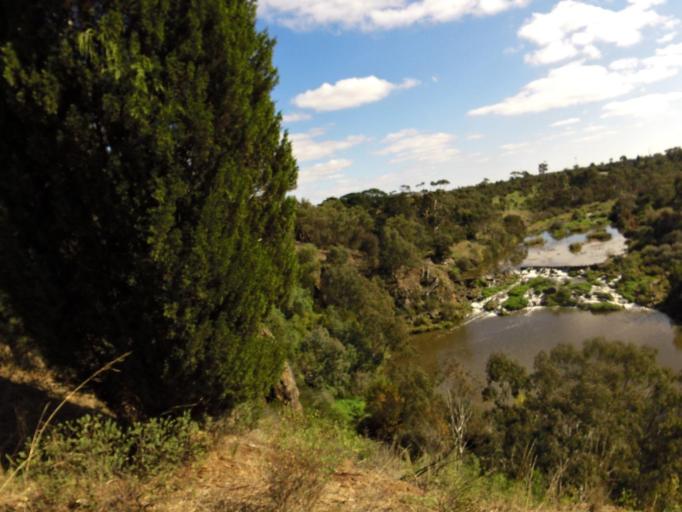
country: AU
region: Victoria
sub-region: Greater Geelong
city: Wandana Heights
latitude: -38.1512
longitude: 144.3082
